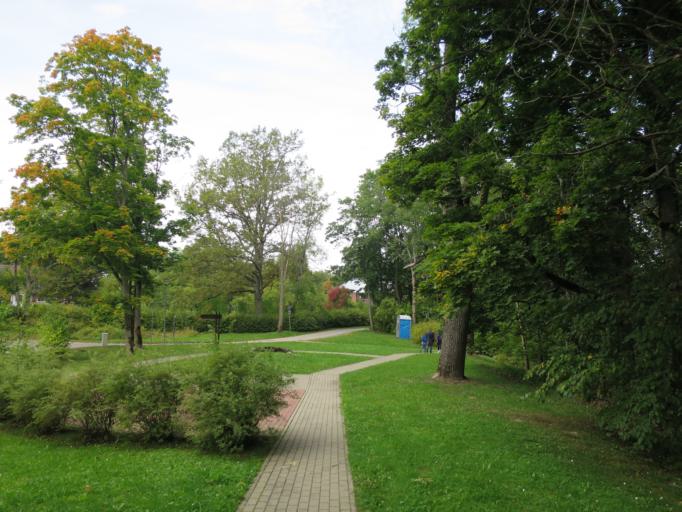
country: LV
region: Sigulda
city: Sigulda
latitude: 57.1698
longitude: 24.8312
